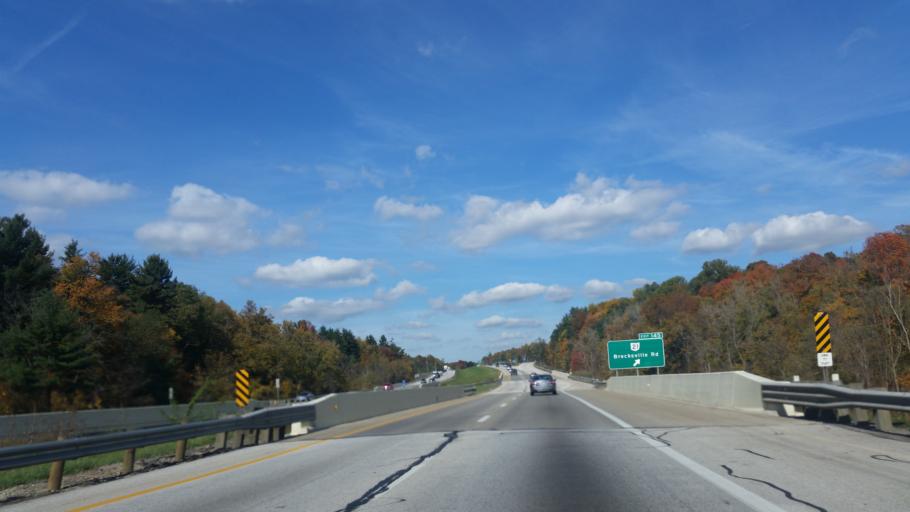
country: US
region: Ohio
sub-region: Summit County
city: Richfield
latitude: 41.2526
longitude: -81.6300
